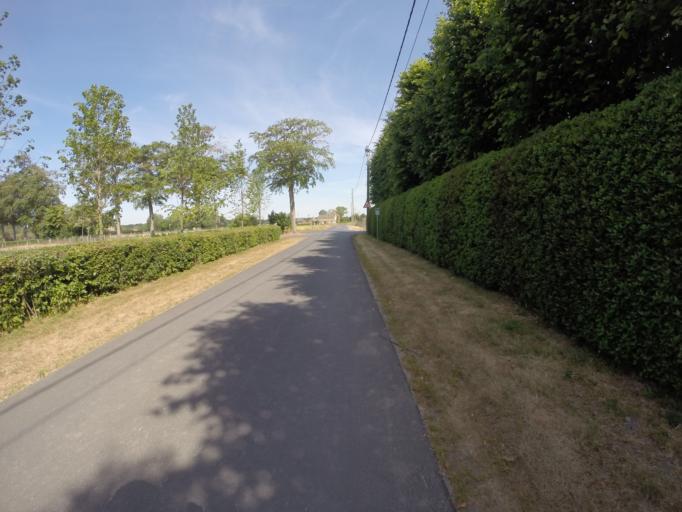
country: BE
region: Flanders
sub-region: Provincie West-Vlaanderen
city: Beernem
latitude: 51.1877
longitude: 3.3258
